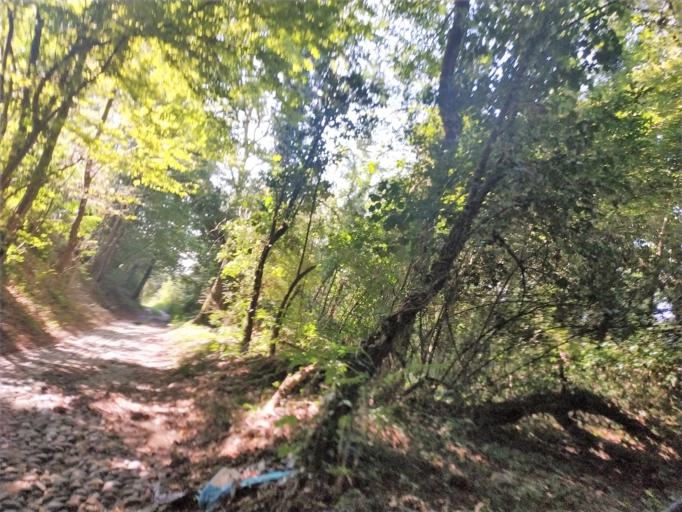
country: IT
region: Piedmont
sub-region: Provincia di Torino
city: Orio Canavese
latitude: 45.3300
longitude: 7.8541
